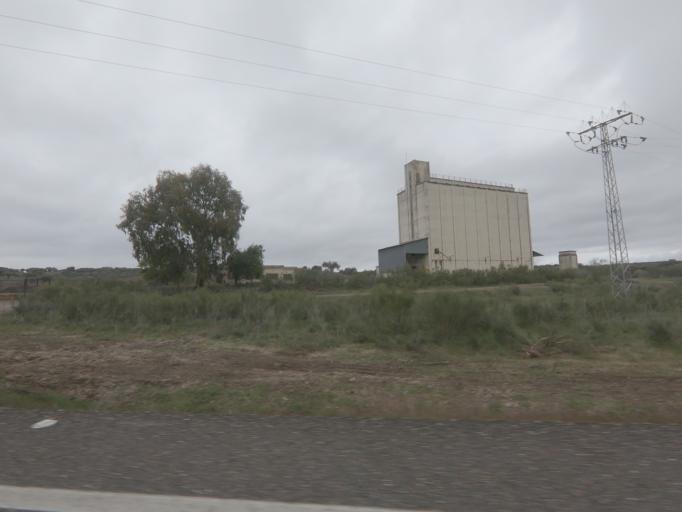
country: ES
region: Extremadura
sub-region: Provincia de Badajoz
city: La Roca de la Sierra
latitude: 39.1171
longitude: -6.6824
